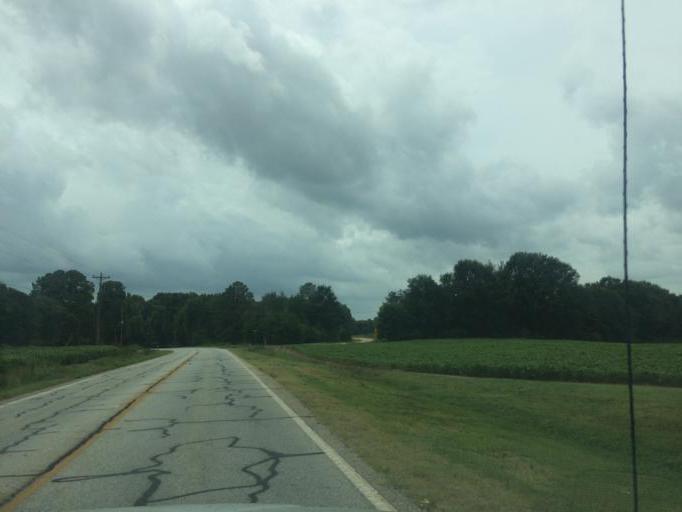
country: US
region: Georgia
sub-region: Hart County
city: Hartwell
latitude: 34.2551
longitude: -82.9000
